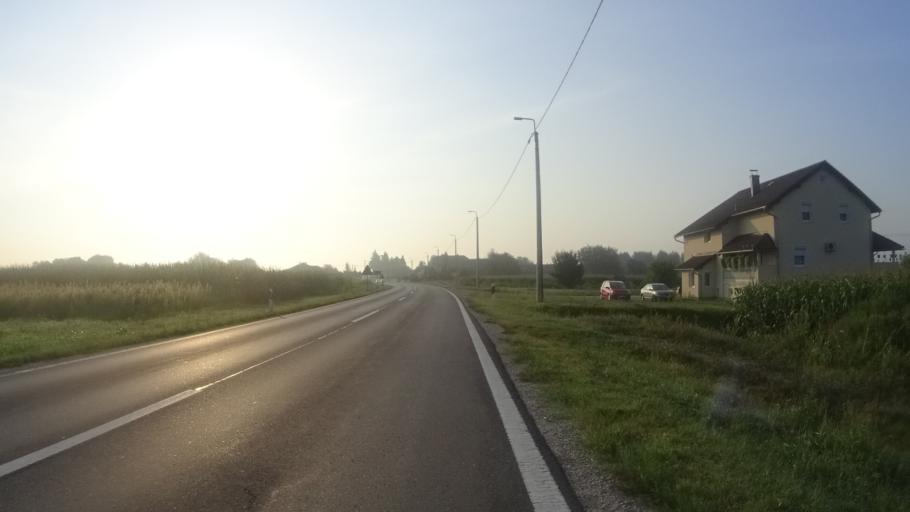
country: HR
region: Varazdinska
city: Petrijanec
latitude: 46.3485
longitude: 16.2092
